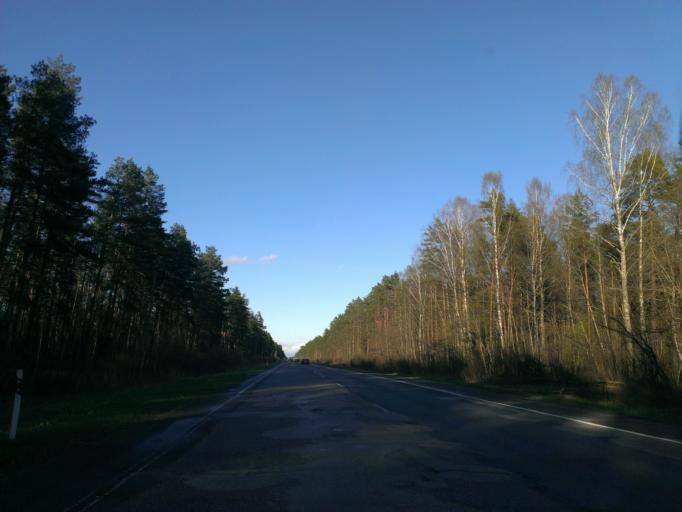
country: LV
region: Incukalns
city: Vangazi
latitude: 57.0727
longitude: 24.5015
